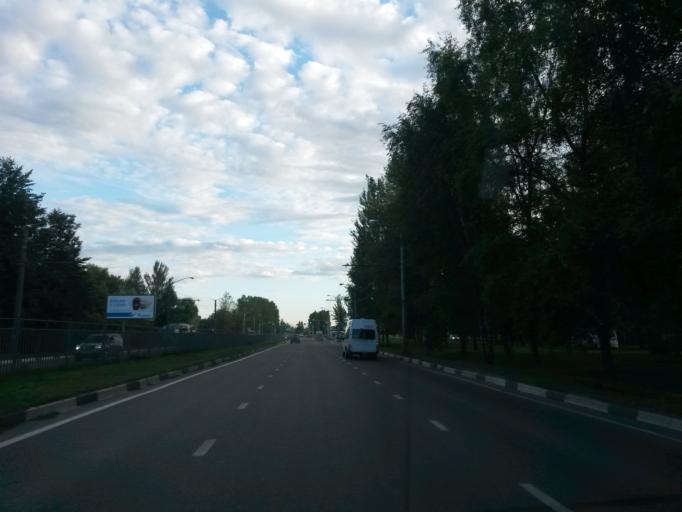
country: RU
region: Jaroslavl
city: Yaroslavl
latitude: 57.6765
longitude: 39.7755
